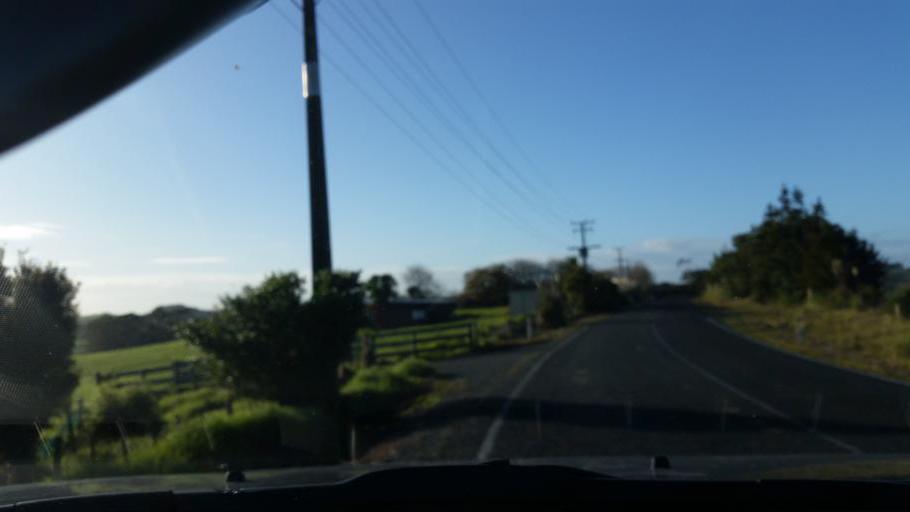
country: NZ
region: Auckland
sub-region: Auckland
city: Wellsford
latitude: -36.1261
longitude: 174.4670
